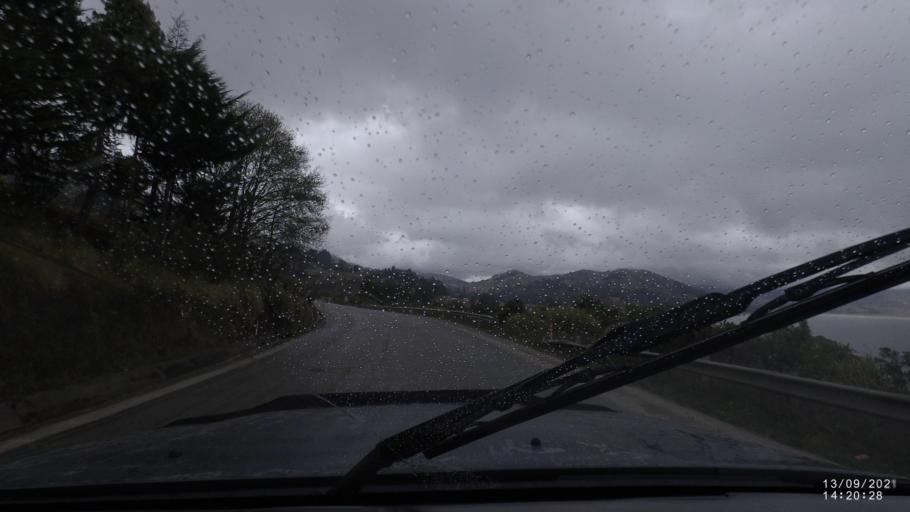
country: BO
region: Cochabamba
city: Colomi
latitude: -17.2524
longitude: -65.8950
